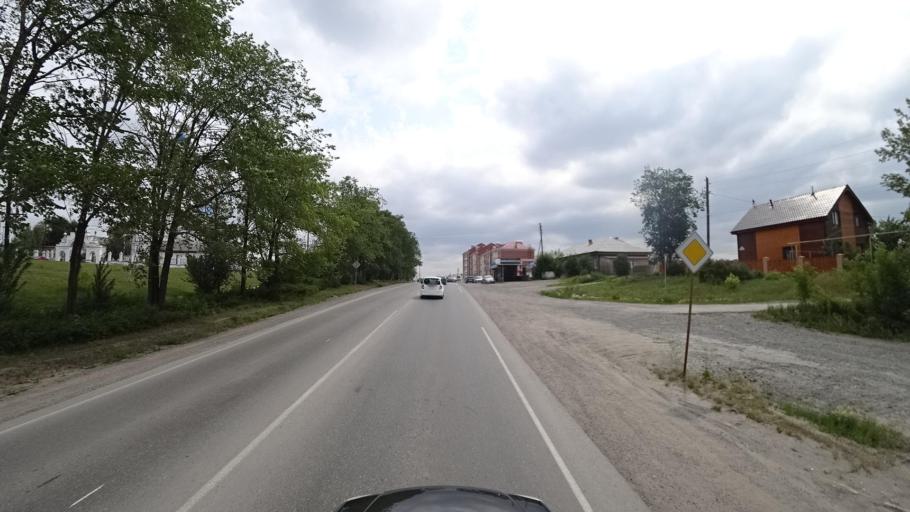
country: RU
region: Sverdlovsk
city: Kamyshlov
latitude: 56.8460
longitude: 62.6877
